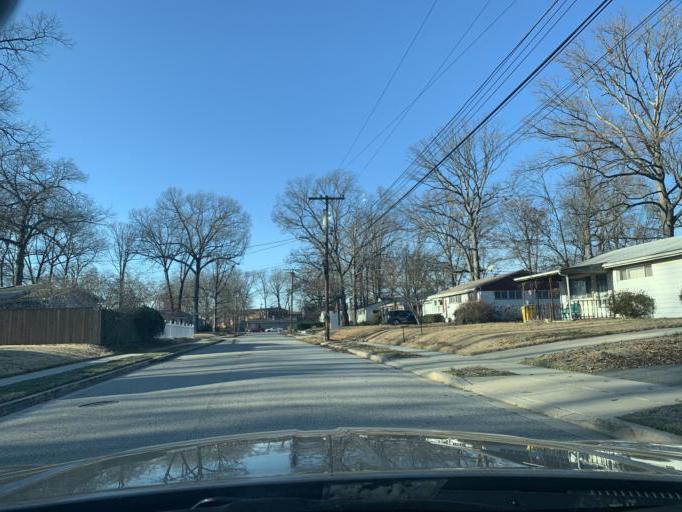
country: US
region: Maryland
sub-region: Anne Arundel County
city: Glen Burnie
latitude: 39.1494
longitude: -76.6292
